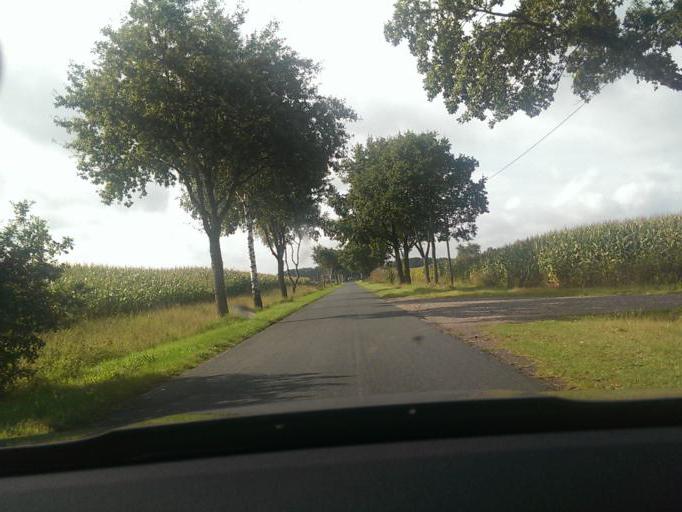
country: DE
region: Lower Saxony
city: Elze
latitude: 52.5746
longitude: 9.7682
